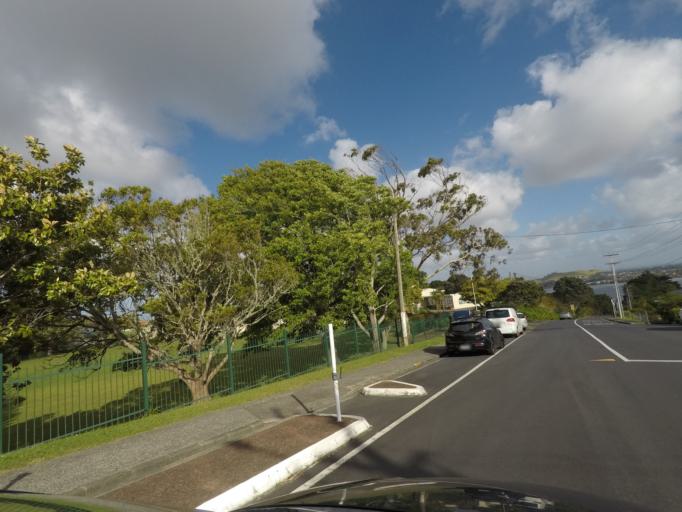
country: NZ
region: Auckland
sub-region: Auckland
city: Auckland
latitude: -36.9224
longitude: 174.7565
